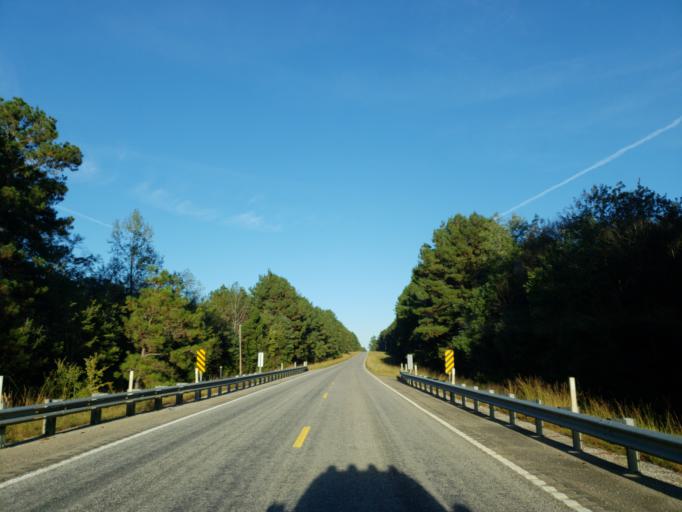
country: US
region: Mississippi
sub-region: Wayne County
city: Belmont
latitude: 31.3942
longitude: -88.6556
